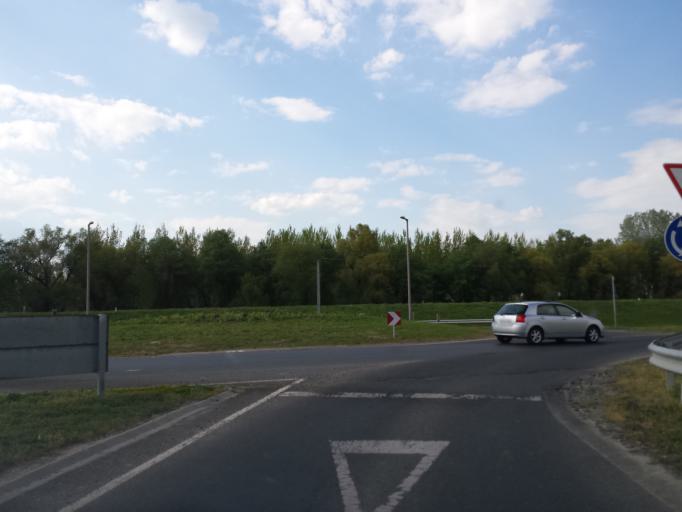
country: HU
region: Csongrad
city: Kiszombor
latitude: 46.1979
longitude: 20.4458
